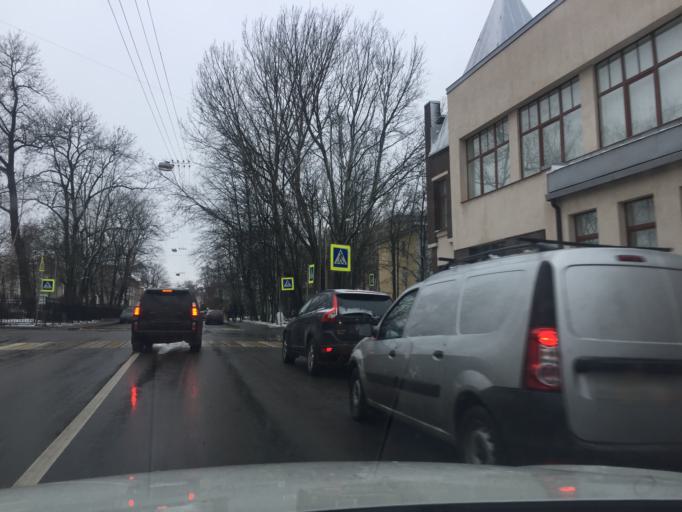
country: RU
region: St.-Petersburg
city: Pushkin
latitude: 59.7187
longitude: 30.4031
